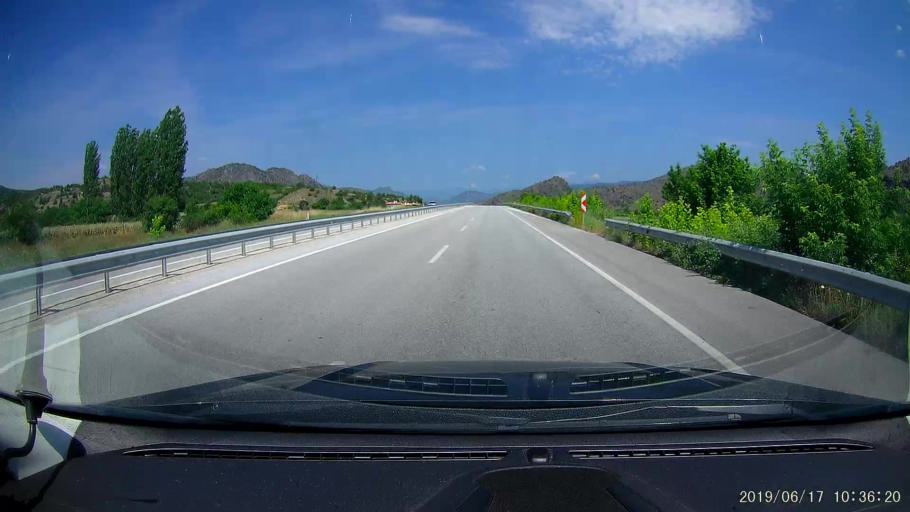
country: TR
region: Corum
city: Osmancik
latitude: 40.9774
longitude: 34.6831
